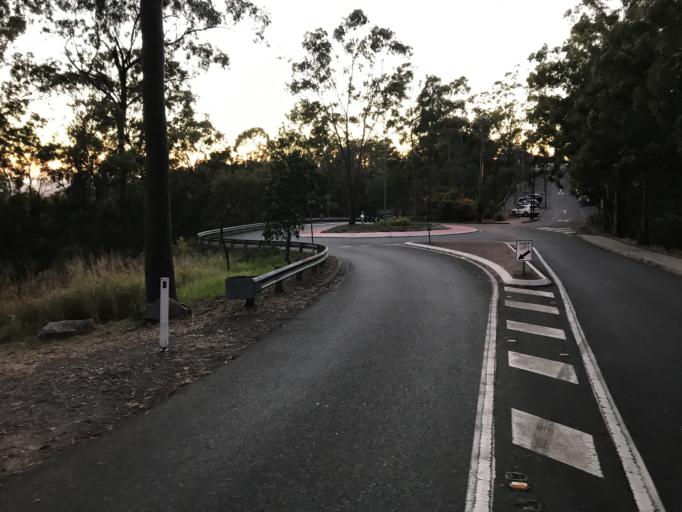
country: AU
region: Queensland
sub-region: Brisbane
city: Taringa
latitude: -27.4847
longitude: 152.9566
